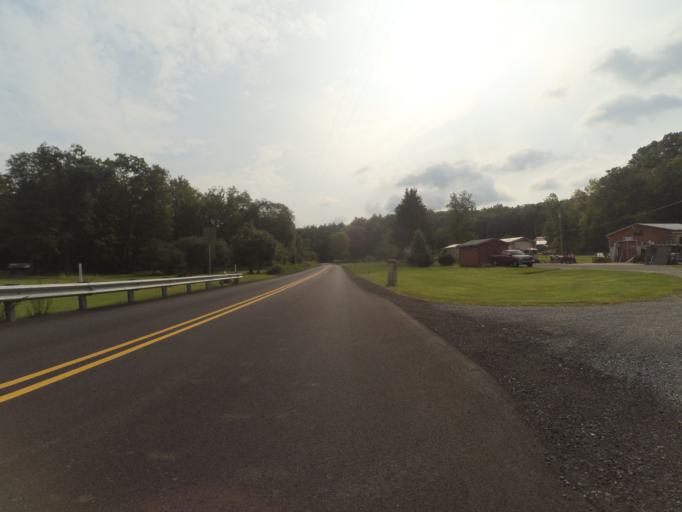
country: US
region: Pennsylvania
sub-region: Centre County
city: Milesburg
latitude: 41.0305
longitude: -77.7369
